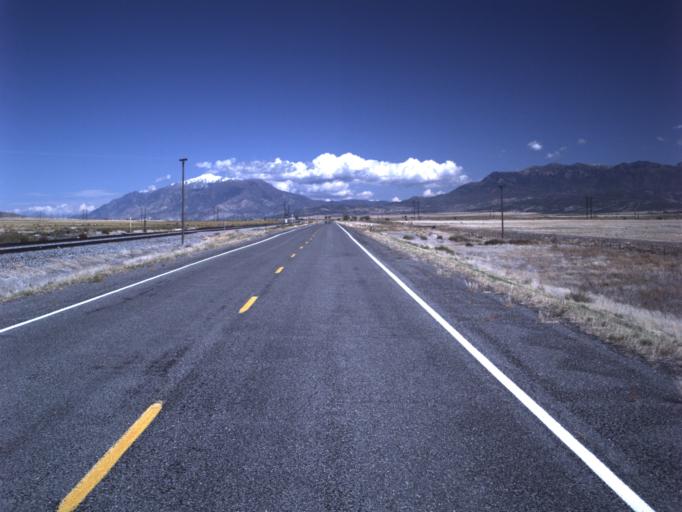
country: US
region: Utah
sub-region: Juab County
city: Nephi
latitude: 39.5192
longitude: -111.9407
